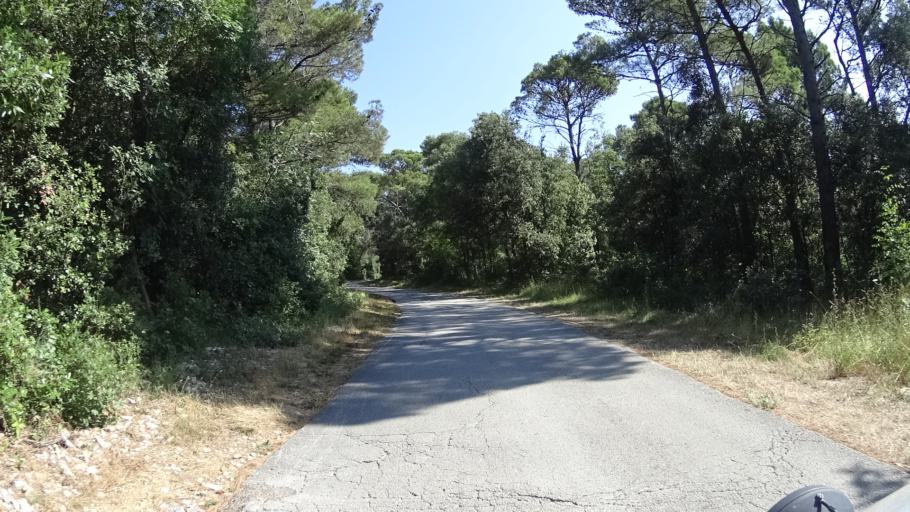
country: HR
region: Istarska
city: Rasa
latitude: 44.9739
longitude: 14.1042
